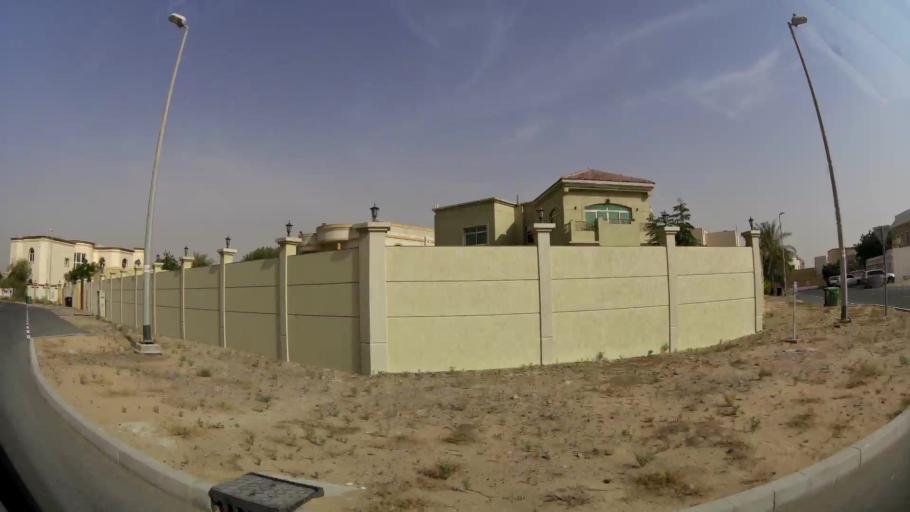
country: AE
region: Ash Shariqah
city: Sharjah
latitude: 25.2560
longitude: 55.4541
